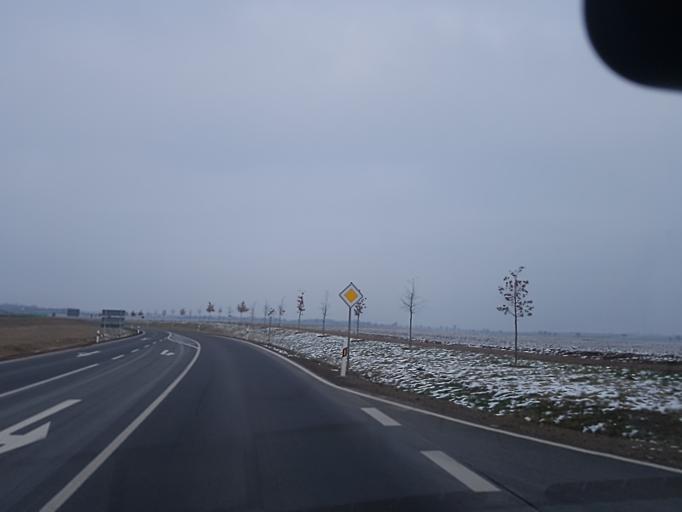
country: DE
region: Saxony
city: Naundorf
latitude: 51.2372
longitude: 13.0857
